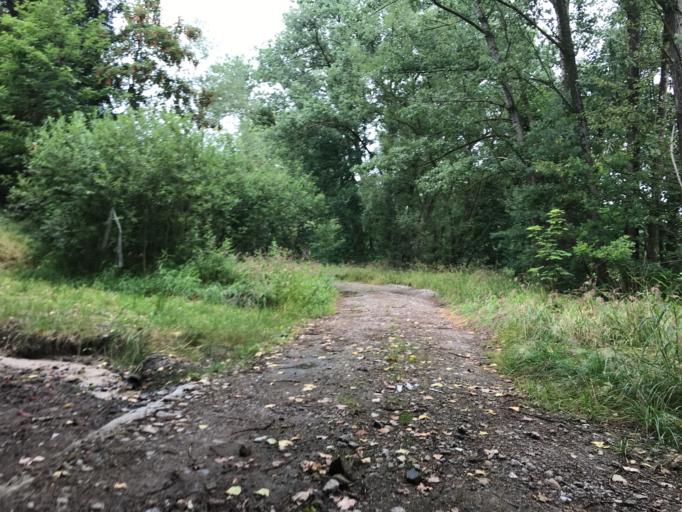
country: CZ
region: Jihocesky
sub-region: Okres Jindrichuv Hradec
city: Trebon
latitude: 49.0104
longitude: 14.7655
